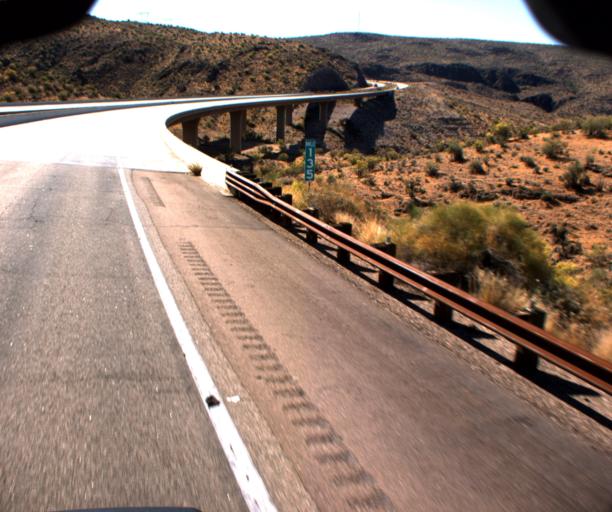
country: US
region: Arizona
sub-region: Yavapai County
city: Bagdad
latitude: 34.5797
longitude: -113.4929
